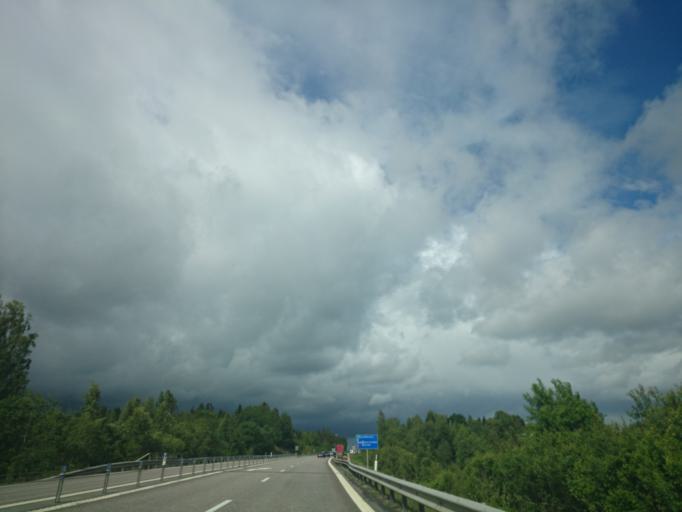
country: SE
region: Vaesternorrland
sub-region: Sundsvalls Kommun
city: Njurundabommen
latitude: 62.2265
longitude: 17.3720
